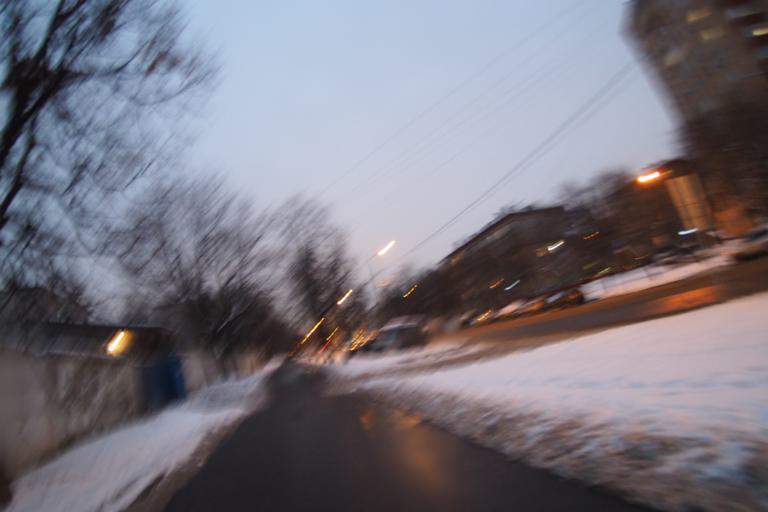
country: RU
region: Moscow
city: Sokol
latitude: 55.7998
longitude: 37.5506
